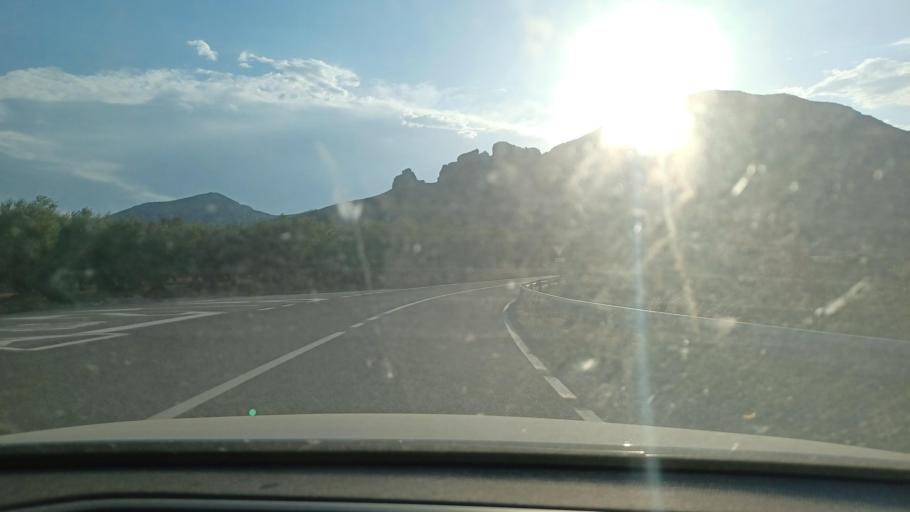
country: ES
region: Catalonia
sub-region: Provincia de Tarragona
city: Mas de Barberans
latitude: 40.7265
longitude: 0.3702
